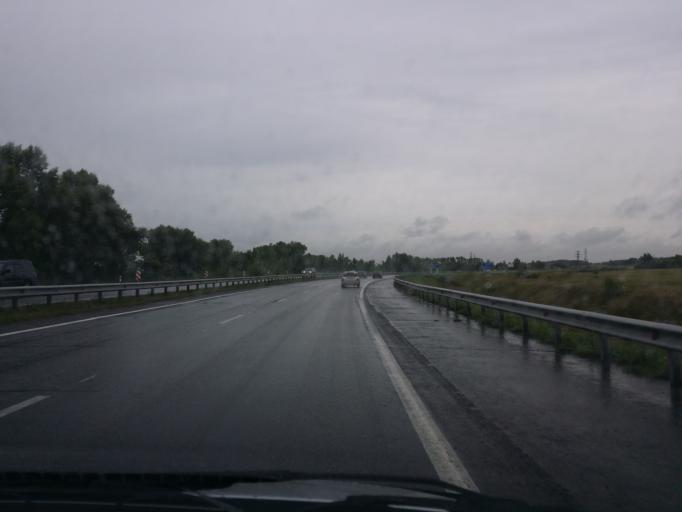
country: RU
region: Altai Krai
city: Novoaltaysk
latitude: 53.3626
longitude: 83.9473
